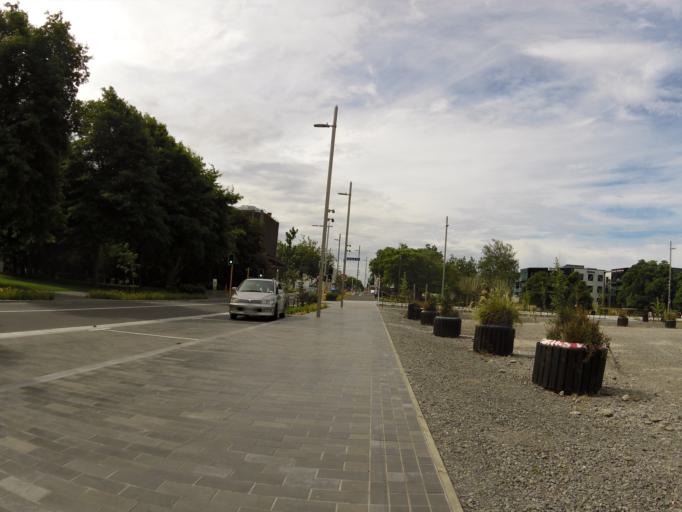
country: NZ
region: Canterbury
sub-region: Christchurch City
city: Christchurch
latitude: -43.5281
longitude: 172.6367
